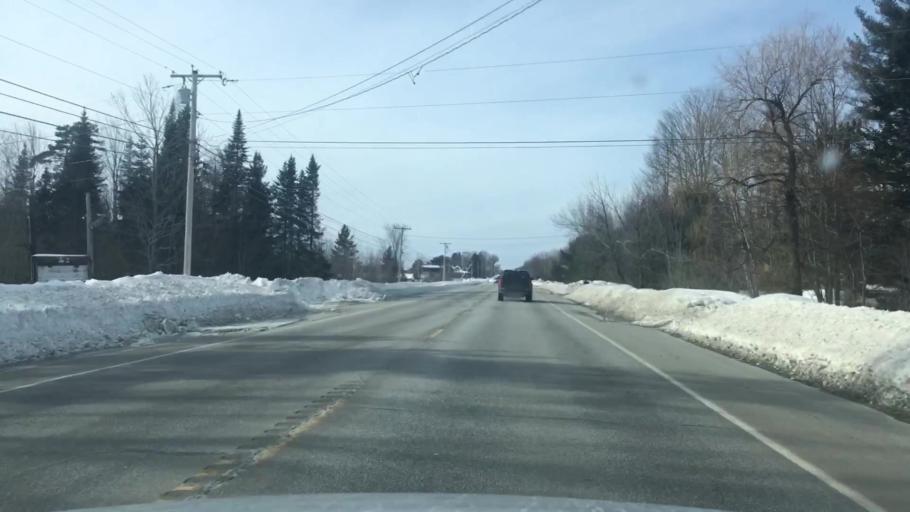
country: US
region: Maine
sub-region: Penobscot County
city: Kenduskeag
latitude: 44.9788
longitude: -68.9927
